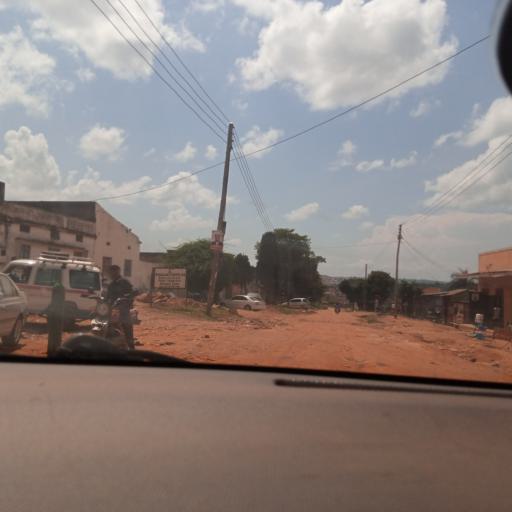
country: UG
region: Central Region
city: Masaka
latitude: -0.3319
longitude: 31.7427
